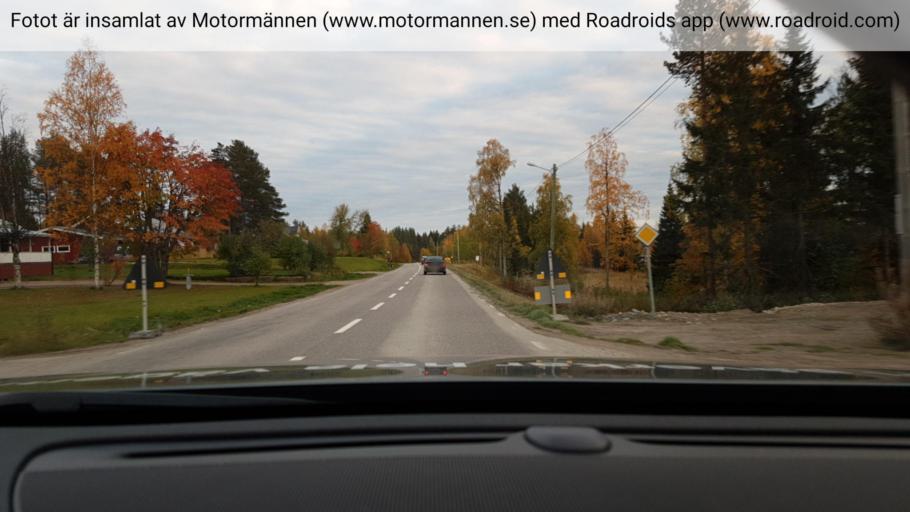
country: SE
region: Norrbotten
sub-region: Jokkmokks Kommun
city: Jokkmokk
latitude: 66.1541
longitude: 19.9817
